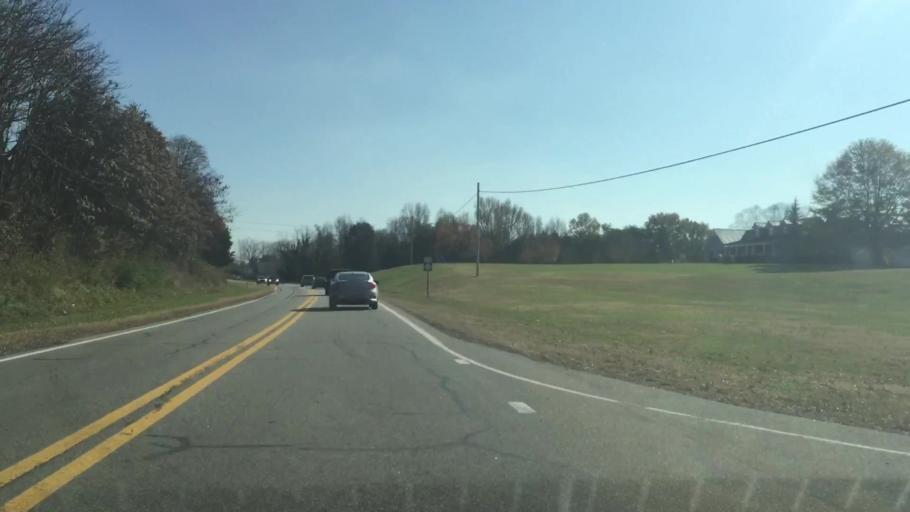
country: US
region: North Carolina
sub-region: Rockingham County
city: Reidsville
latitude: 36.2853
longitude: -79.6041
